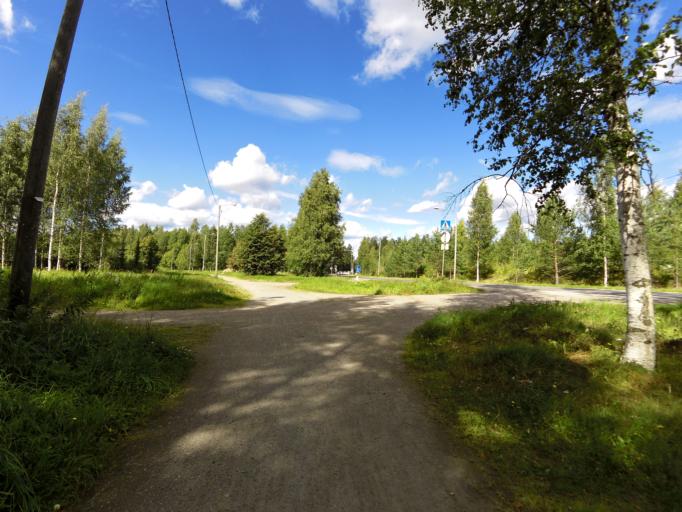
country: FI
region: Pirkanmaa
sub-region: Tampere
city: Yloejaervi
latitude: 61.5135
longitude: 23.6164
